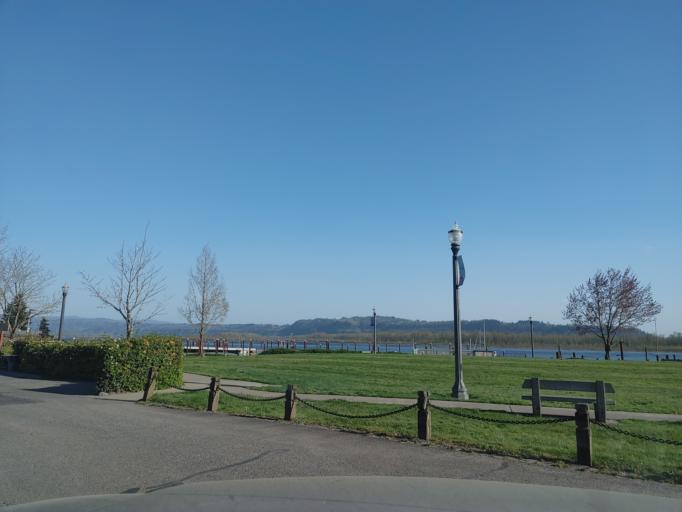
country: US
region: Washington
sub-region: Clark County
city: Camas
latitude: 45.5787
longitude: -122.3818
